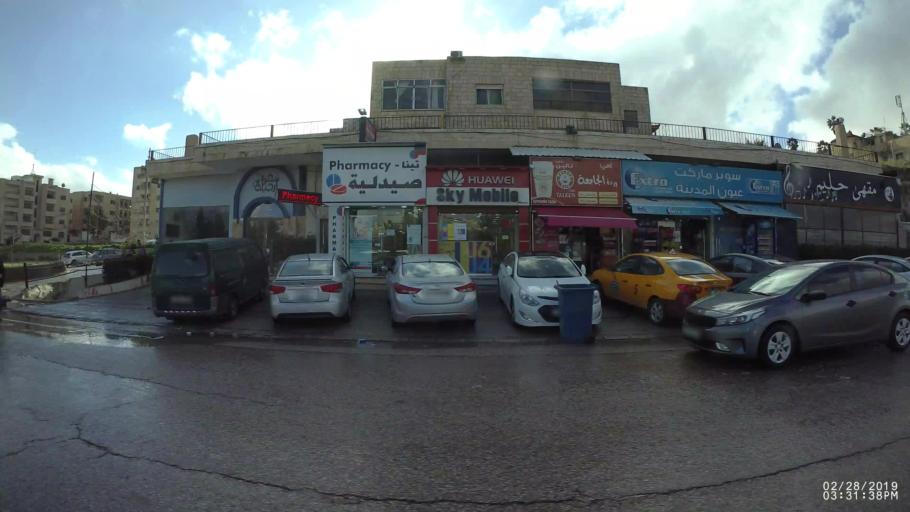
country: JO
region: Amman
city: Al Jubayhah
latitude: 32.0093
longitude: 35.8713
